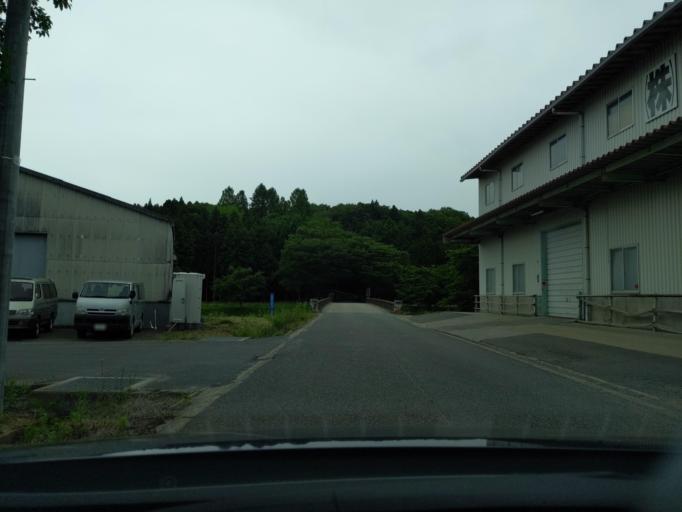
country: JP
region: Fukushima
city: Koriyama
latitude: 37.3597
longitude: 140.3449
